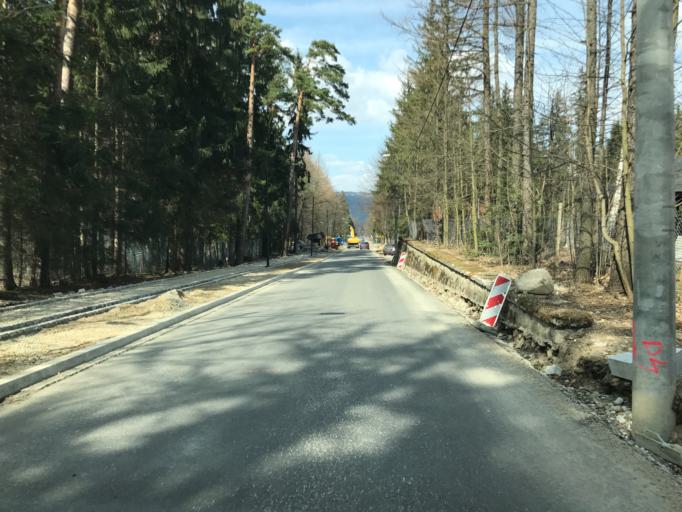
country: PL
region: Lesser Poland Voivodeship
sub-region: Powiat tatrzanski
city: Zakopane
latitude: 49.2830
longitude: 19.9758
